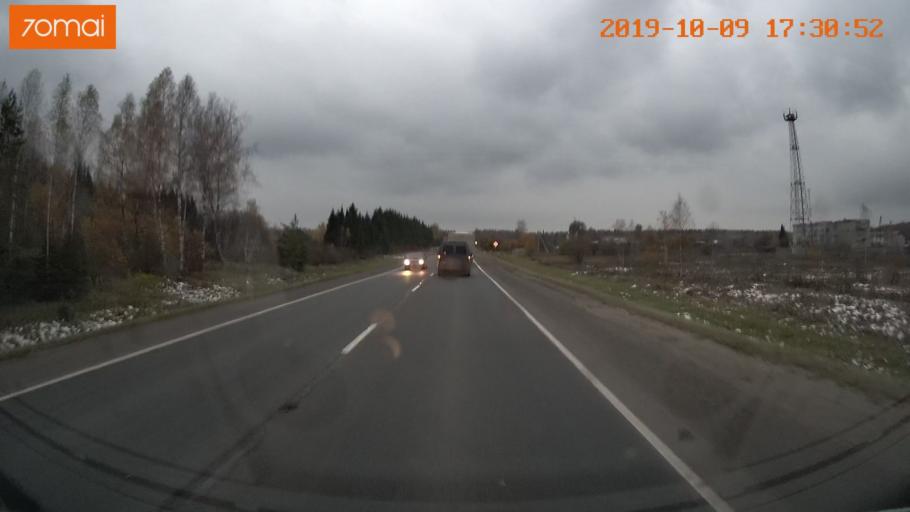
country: RU
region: Ivanovo
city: Bogorodskoye
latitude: 57.1395
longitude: 41.0450
